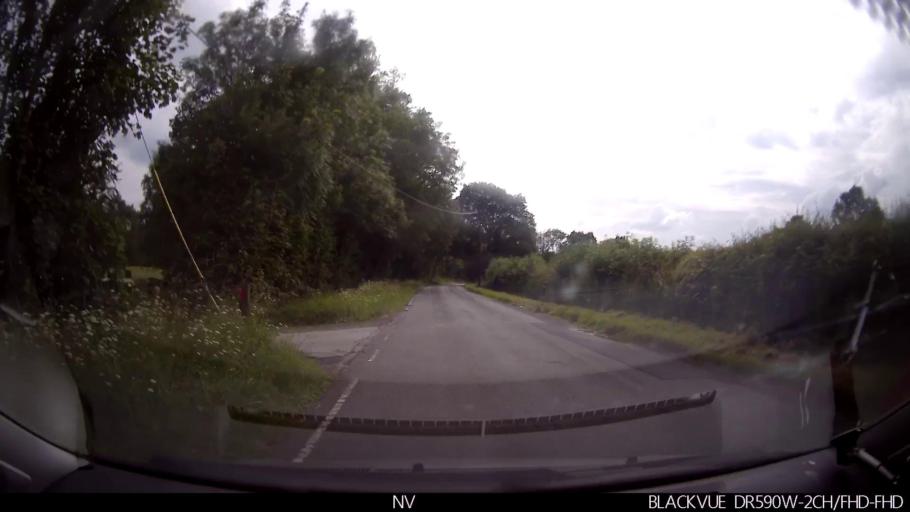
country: GB
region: England
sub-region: North Yorkshire
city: Strensall
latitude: 54.0384
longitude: -1.0192
